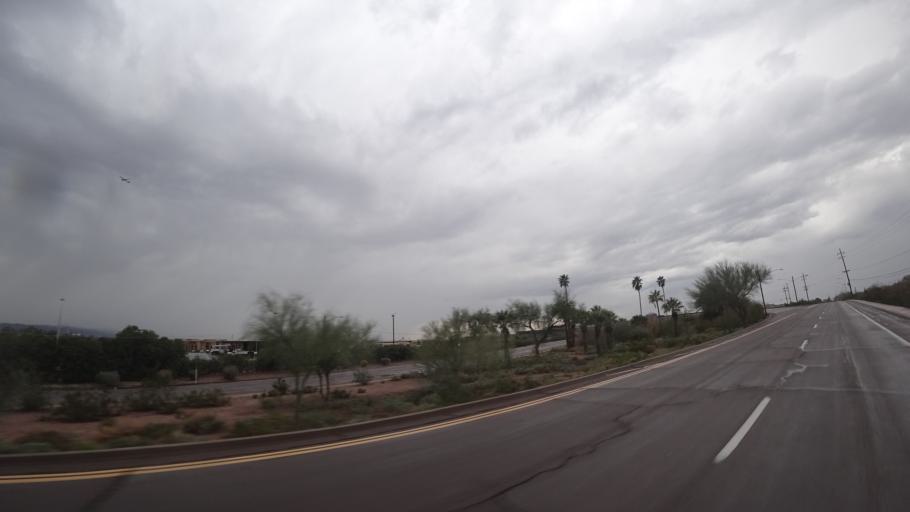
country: US
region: Arizona
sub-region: Maricopa County
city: Tempe Junction
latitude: 33.4415
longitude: -111.9459
